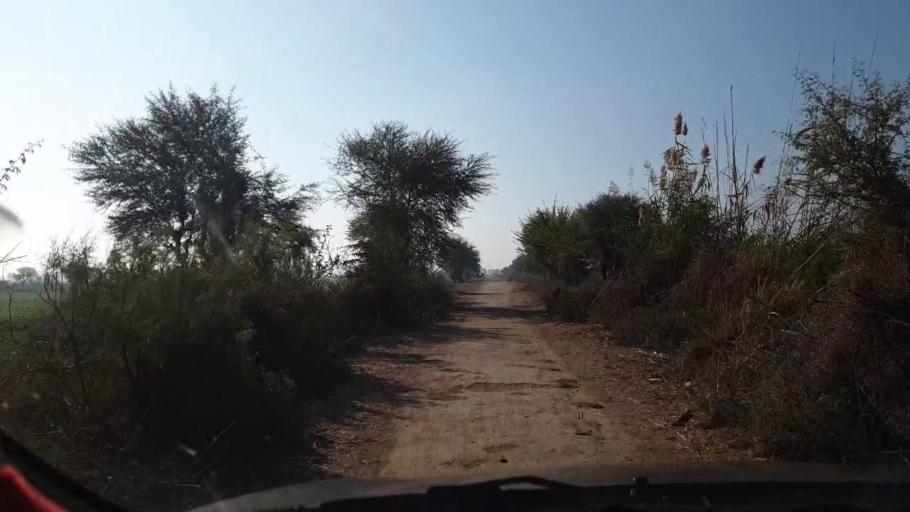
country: PK
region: Sindh
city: Sinjhoro
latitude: 26.0227
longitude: 68.8056
